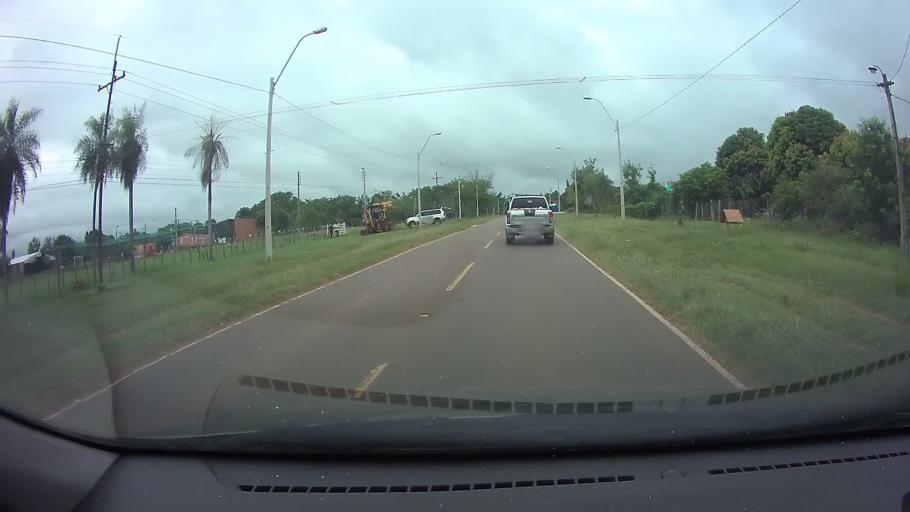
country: PY
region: Central
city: Nueva Italia
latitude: -25.6095
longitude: -57.4749
